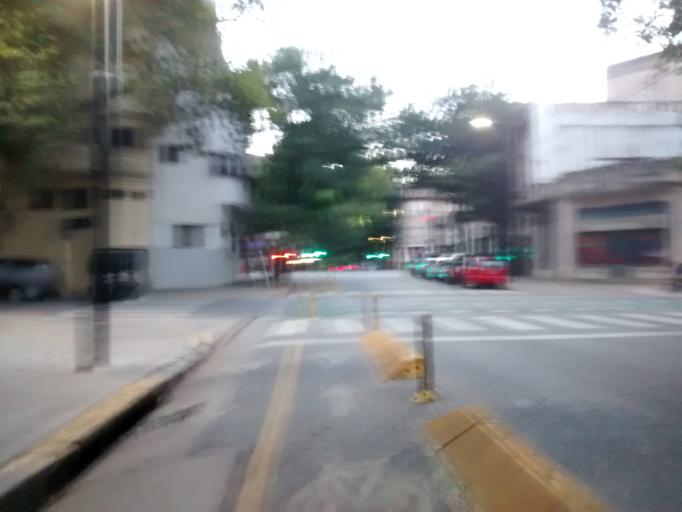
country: AR
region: Buenos Aires F.D.
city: Villa Santa Rita
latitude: -34.6053
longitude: -58.4533
